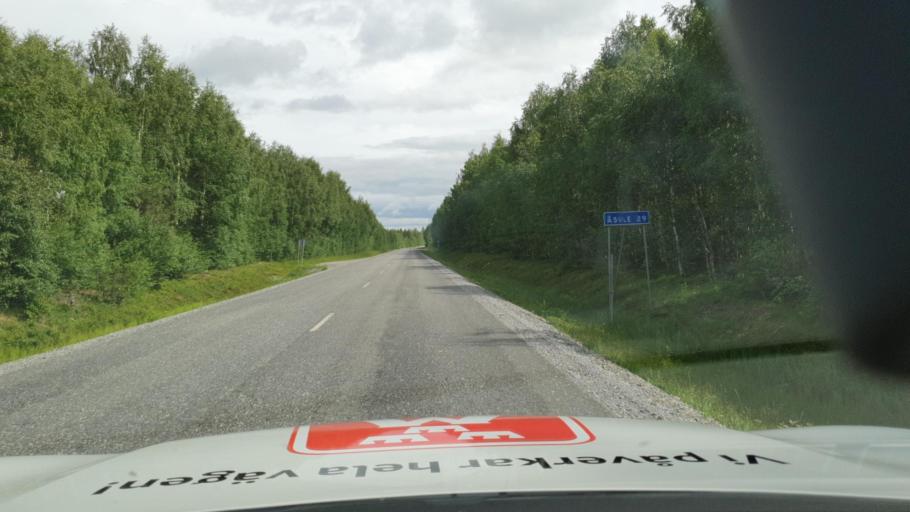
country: SE
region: Vaesterbotten
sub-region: Dorotea Kommun
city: Dorotea
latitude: 64.2273
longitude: 16.8316
